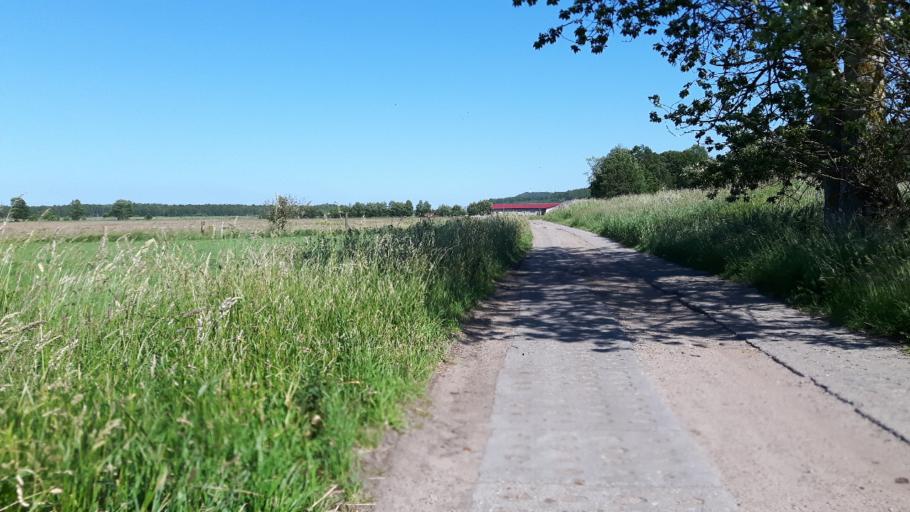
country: PL
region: Pomeranian Voivodeship
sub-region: Powiat slupski
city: Glowczyce
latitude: 54.6421
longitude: 17.3700
